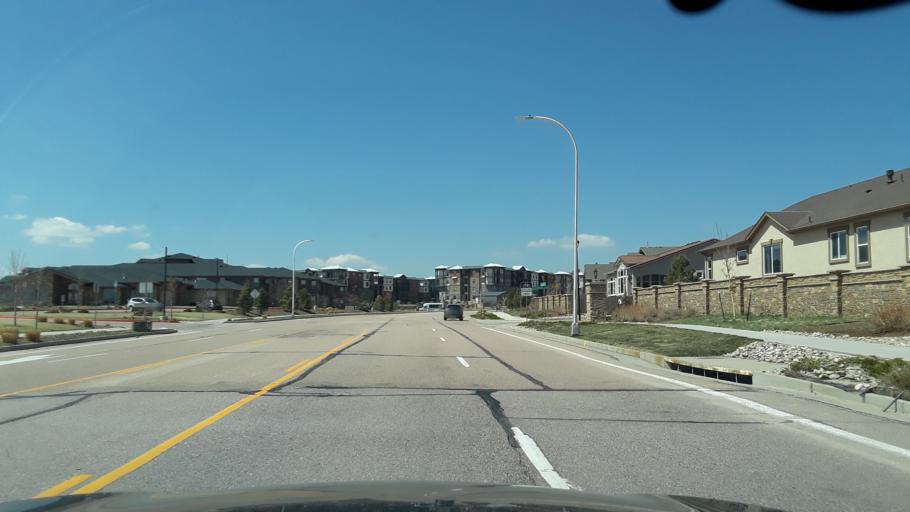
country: US
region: Colorado
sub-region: El Paso County
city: Black Forest
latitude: 38.9618
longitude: -104.7286
